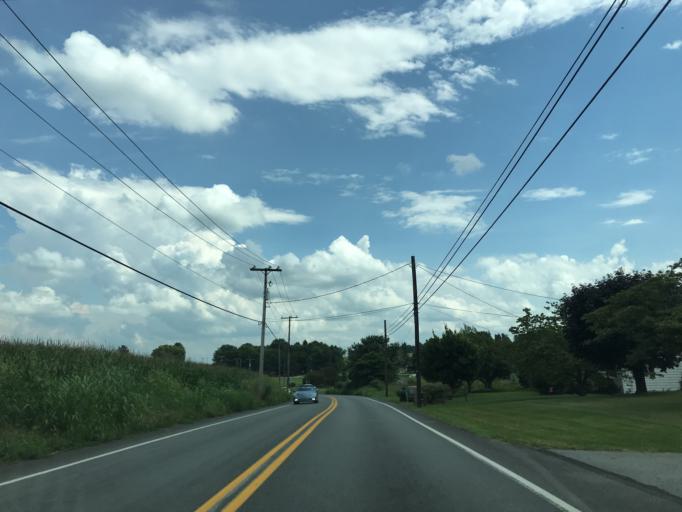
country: US
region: Pennsylvania
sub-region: York County
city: Windsor
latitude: 39.8826
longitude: -76.5393
